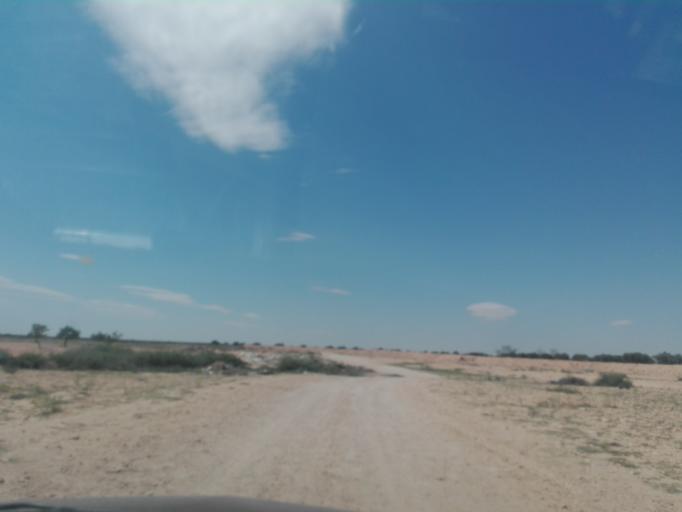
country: TN
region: Safaqis
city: Sfax
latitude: 34.6692
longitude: 10.5718
